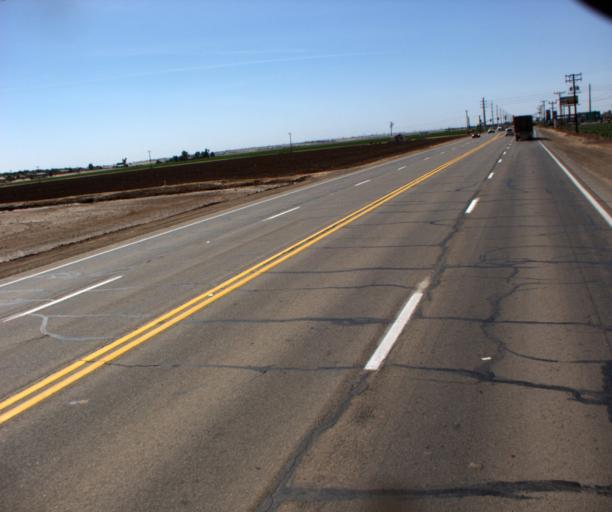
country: US
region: Arizona
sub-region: Yuma County
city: Fortuna Foothills
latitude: 32.6993
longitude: -114.5095
